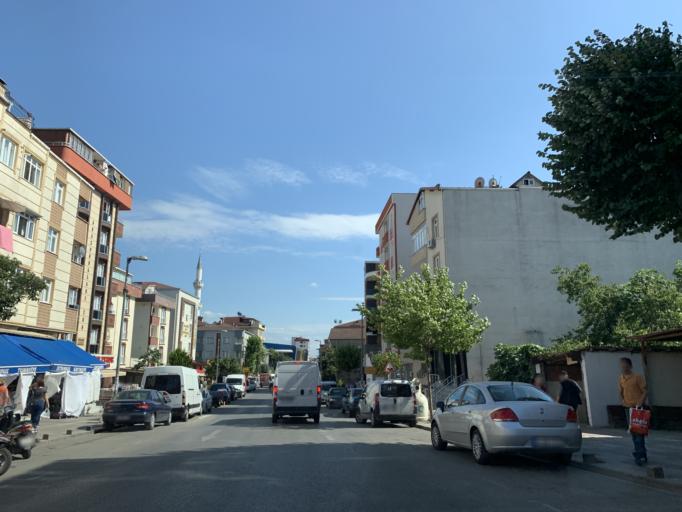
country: TR
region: Istanbul
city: Pendik
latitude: 40.8833
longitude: 29.2724
